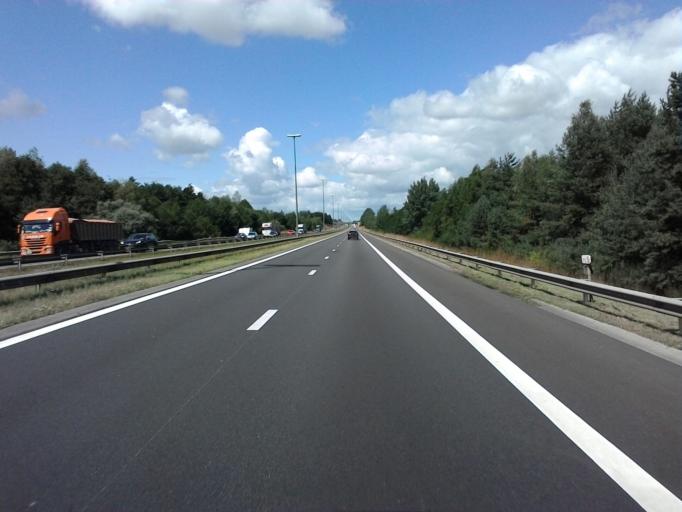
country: BE
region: Wallonia
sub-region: Province du Luxembourg
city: Attert
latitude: 49.6914
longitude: 5.7266
